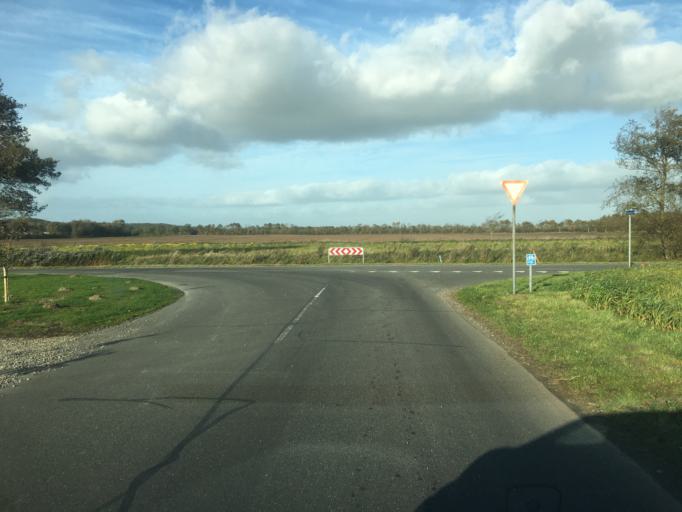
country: DK
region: South Denmark
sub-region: Tonder Kommune
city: Logumkloster
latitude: 55.0732
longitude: 8.9431
